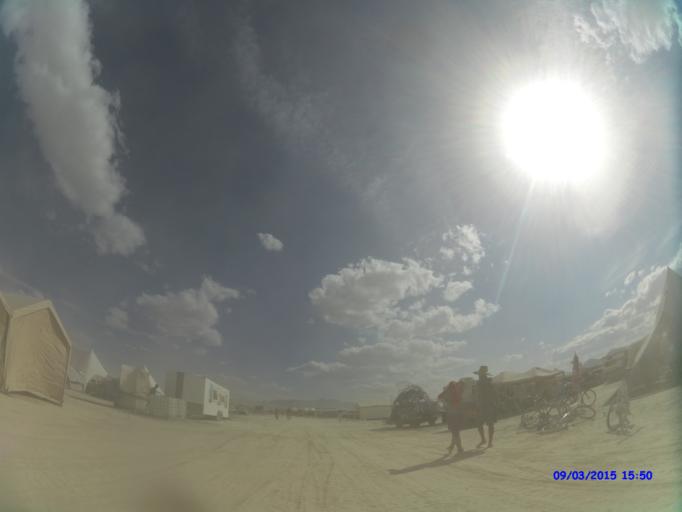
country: US
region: Nevada
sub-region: Pershing County
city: Lovelock
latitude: 40.7874
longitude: -119.2188
